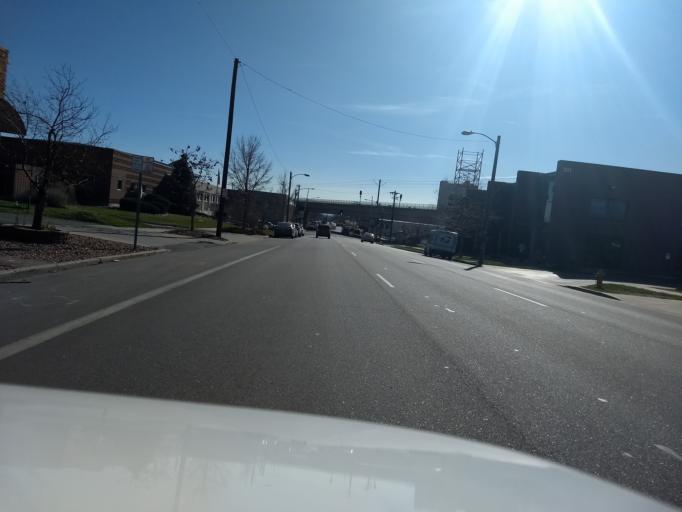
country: US
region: Colorado
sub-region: Denver County
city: Denver
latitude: 39.7219
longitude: -105.0001
